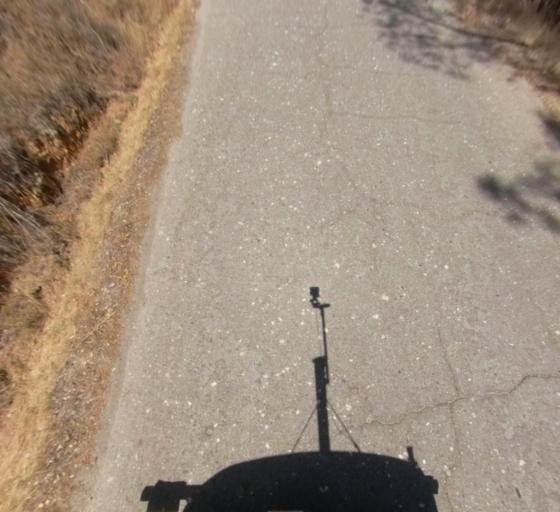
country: US
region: California
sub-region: Fresno County
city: Auberry
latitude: 37.1457
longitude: -119.4985
